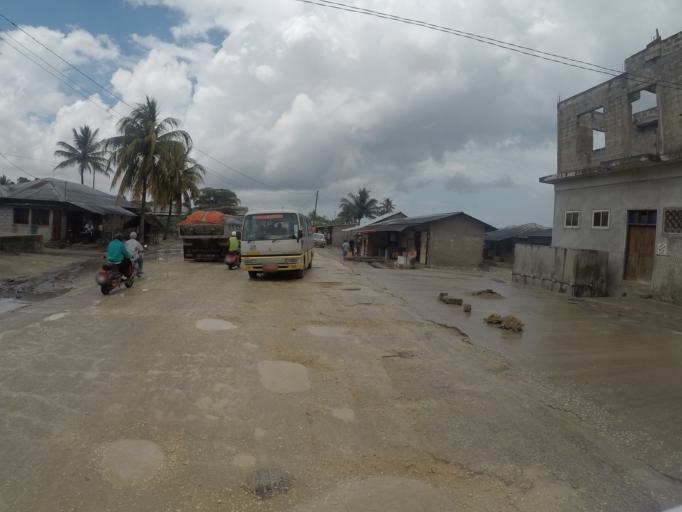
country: TZ
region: Zanzibar Central/South
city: Koani
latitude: -6.0811
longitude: 39.2221
